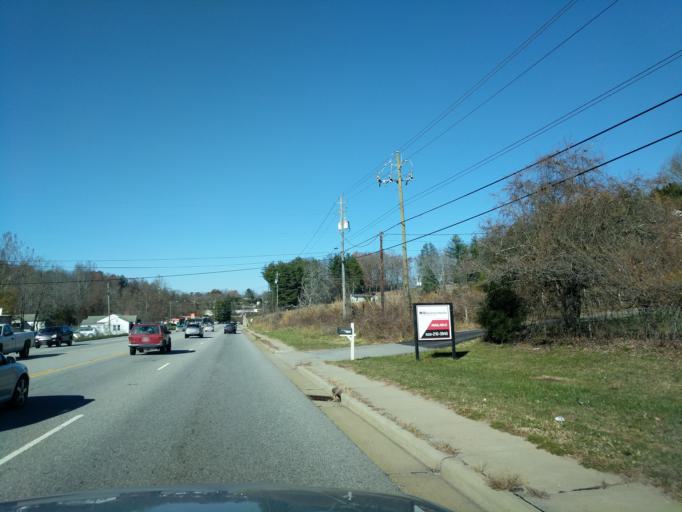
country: US
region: North Carolina
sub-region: Buncombe County
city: Biltmore Forest
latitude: 35.5420
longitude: -82.5210
